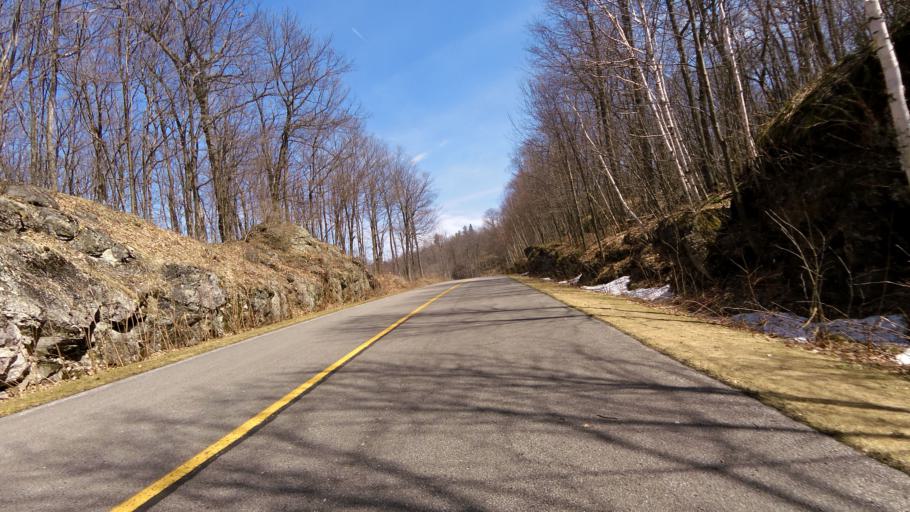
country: CA
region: Quebec
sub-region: Outaouais
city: Gatineau
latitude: 45.4959
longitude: -75.8701
